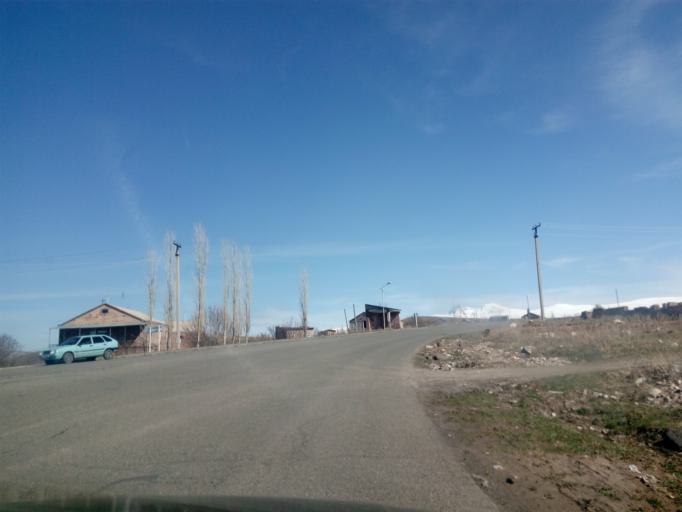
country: AM
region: Shirak
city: Horrom
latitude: 40.6622
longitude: 43.8856
